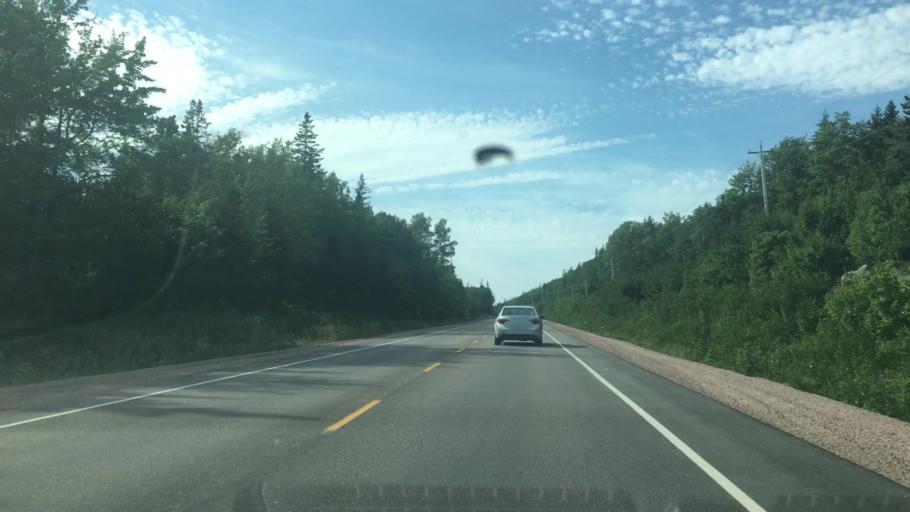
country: CA
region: Nova Scotia
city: Sydney Mines
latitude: 46.8157
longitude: -60.3426
